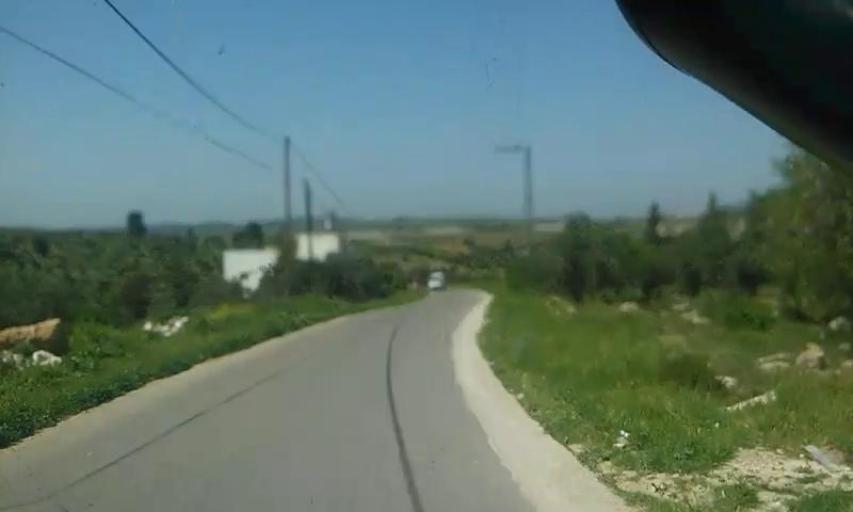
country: PS
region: West Bank
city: Al Majd
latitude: 31.4849
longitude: 34.9446
